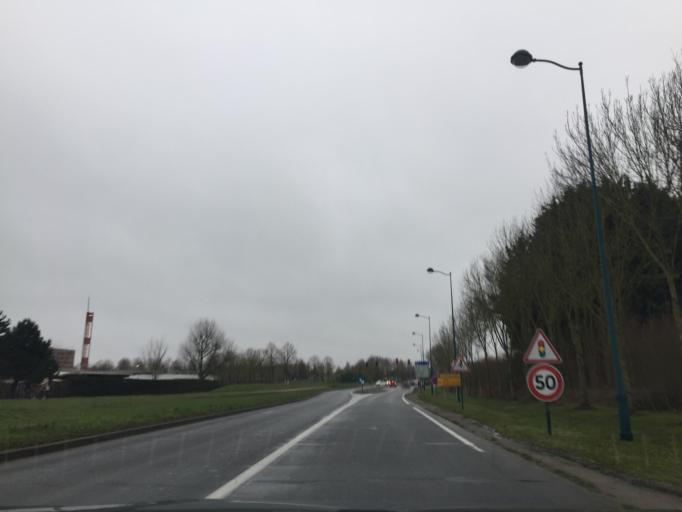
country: FR
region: Ile-de-France
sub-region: Departement de Seine-et-Marne
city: Magny-le-Hongre
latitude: 48.8634
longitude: 2.8075
